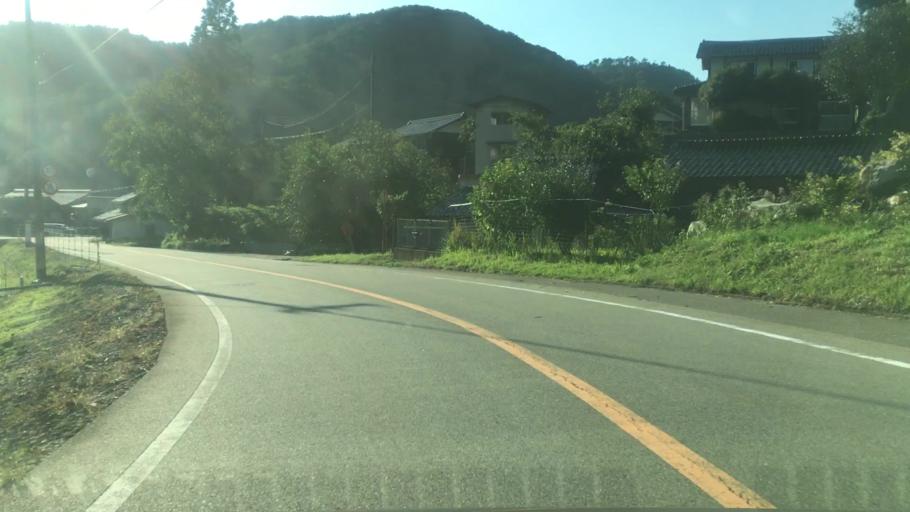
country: JP
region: Hyogo
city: Toyooka
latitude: 35.6216
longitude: 134.8660
